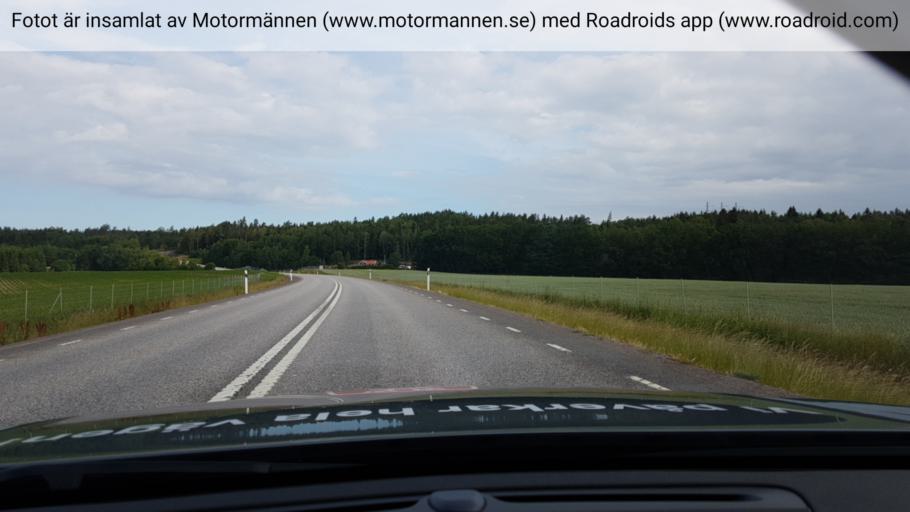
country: SE
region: OEstergoetland
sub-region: Motala Kommun
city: Borensberg
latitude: 58.5567
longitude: 15.3206
